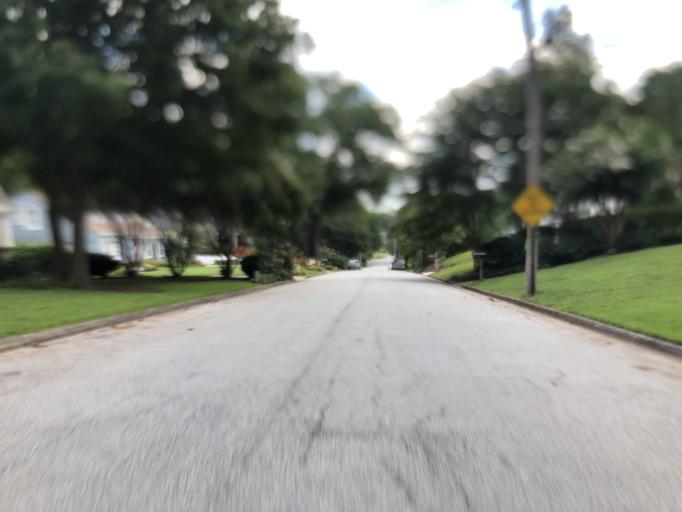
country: US
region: Georgia
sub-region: DeKalb County
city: North Decatur
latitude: 33.7796
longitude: -84.3076
